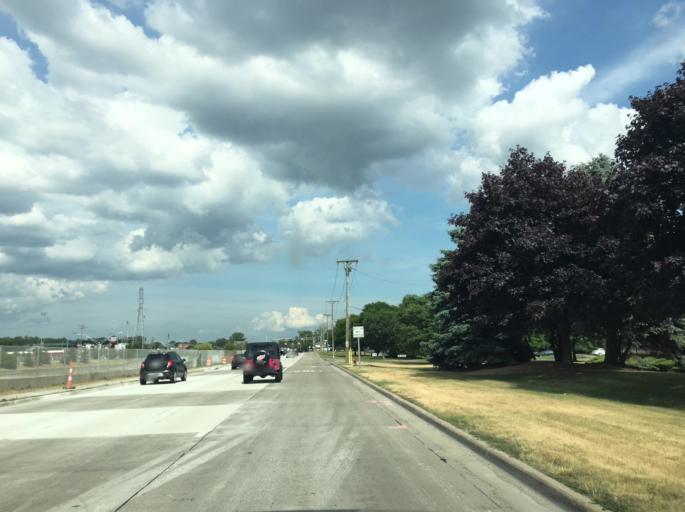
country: US
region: Michigan
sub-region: Macomb County
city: Utica
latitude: 42.6246
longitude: -83.0456
